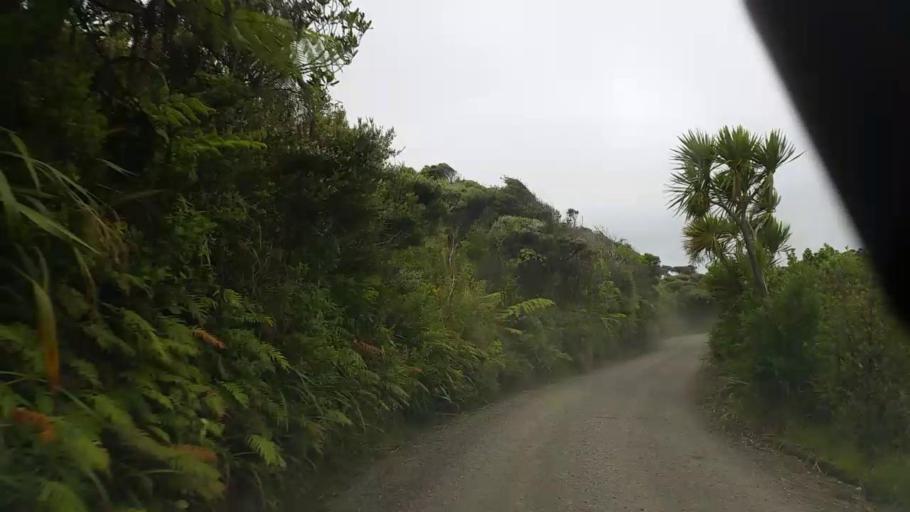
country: NZ
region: Auckland
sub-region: Auckland
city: Muriwai Beach
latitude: -36.9281
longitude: 174.4721
